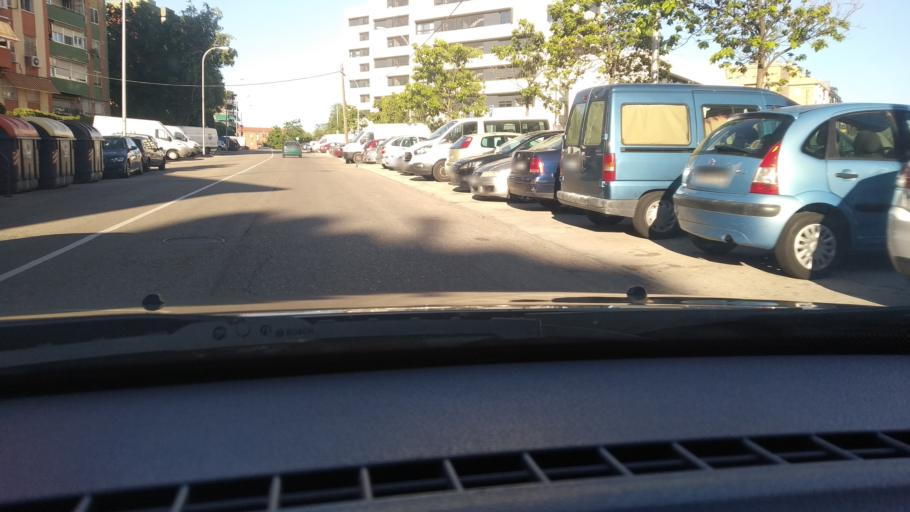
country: ES
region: Madrid
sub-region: Provincia de Madrid
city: Villa de Vallecas
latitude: 40.3772
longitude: -3.6288
